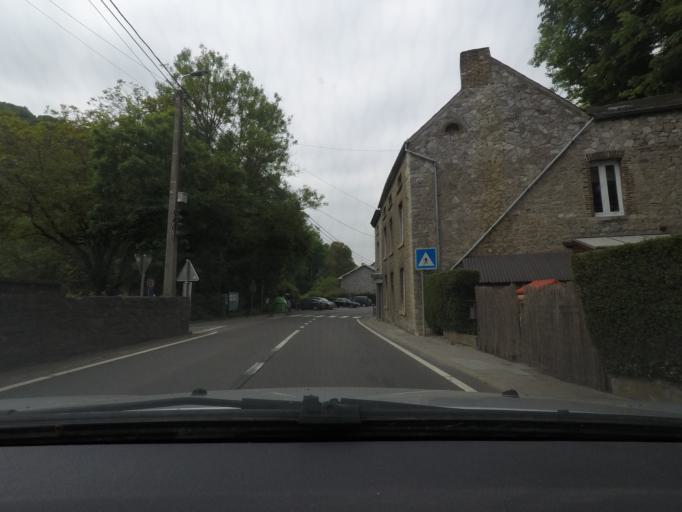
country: BE
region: Wallonia
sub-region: Province de Namur
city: Noville-les-Bois
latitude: 50.4658
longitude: 4.9941
